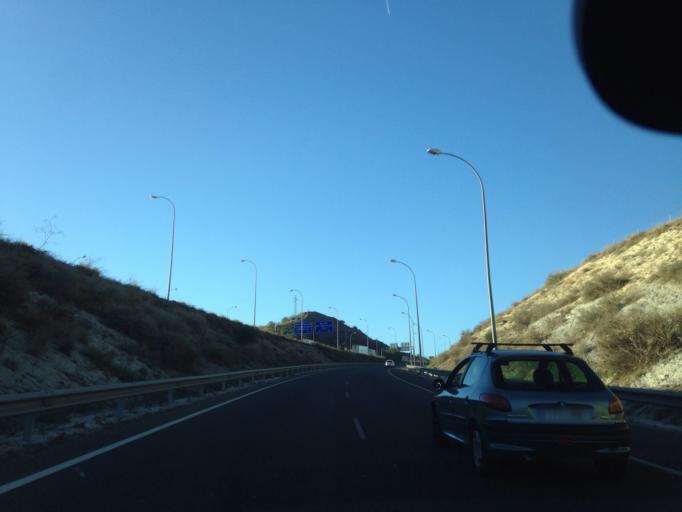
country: ES
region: Andalusia
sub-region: Provincia de Malaga
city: Malaga
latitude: 36.7512
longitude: -4.4320
